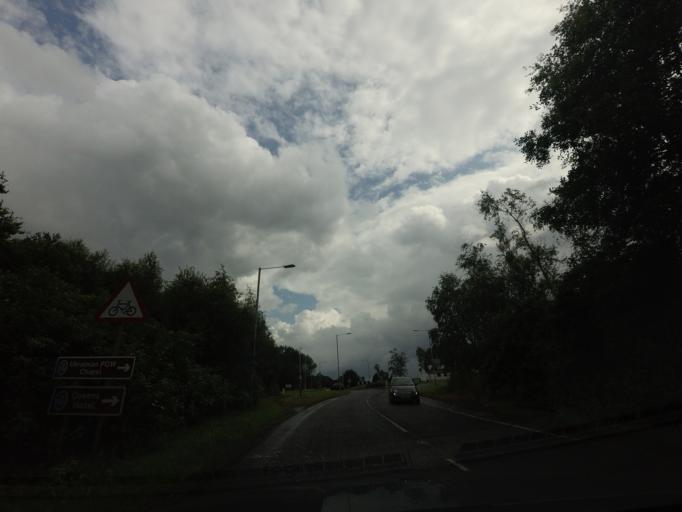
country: GB
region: Scotland
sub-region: Dumfries and Galloway
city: Lockerbie
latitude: 55.1101
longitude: -3.3531
